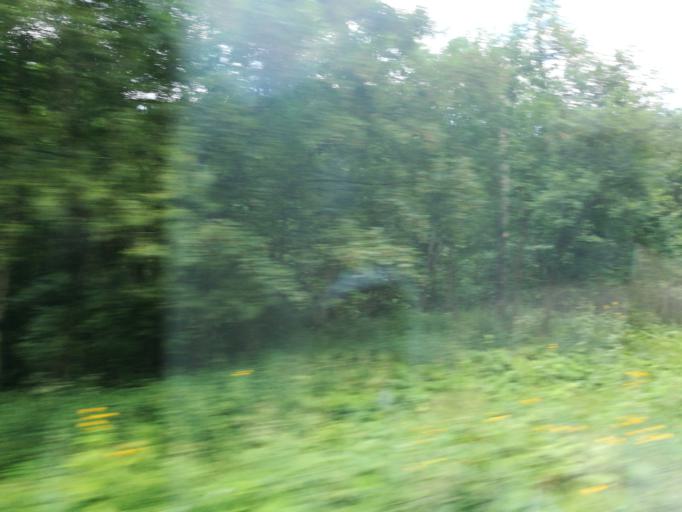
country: RO
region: Brasov
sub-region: Oras Predeal
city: Predeal
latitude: 45.5198
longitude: 25.6092
